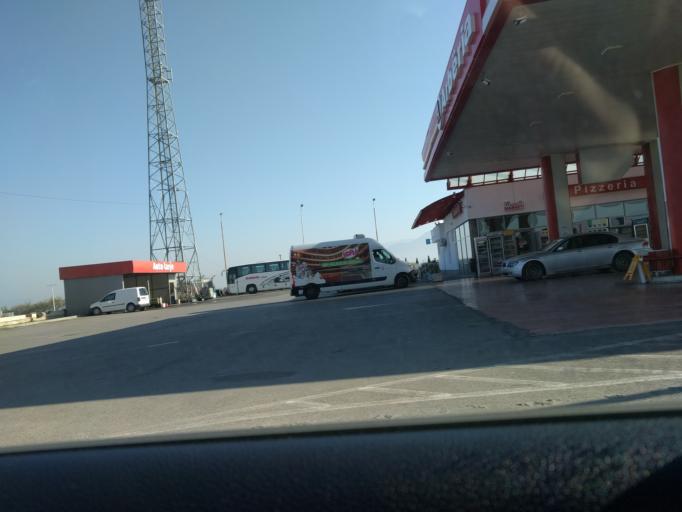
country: XK
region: Prizren
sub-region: Prizren
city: Prizren
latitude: 42.2481
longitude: 20.7205
